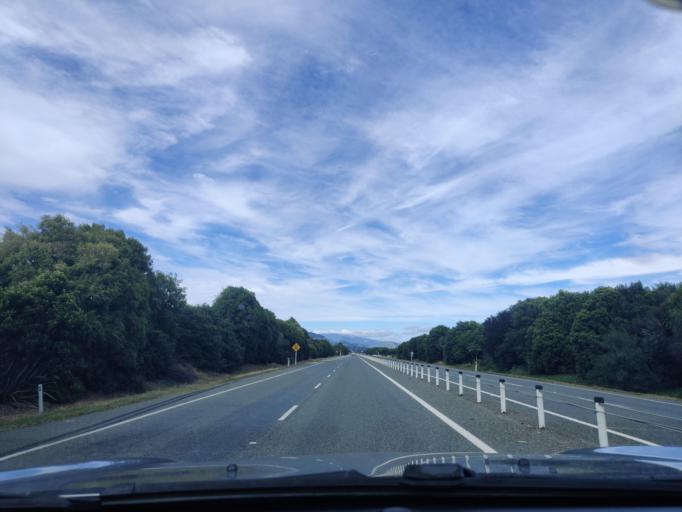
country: NZ
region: Tasman
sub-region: Tasman District
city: Richmond
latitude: -41.3099
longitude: 173.2189
